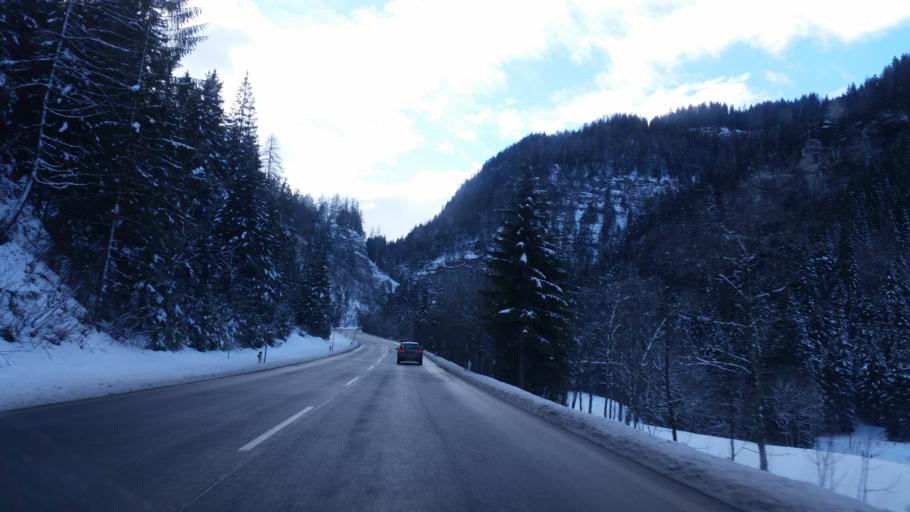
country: AT
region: Salzburg
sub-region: Politischer Bezirk Sankt Johann im Pongau
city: Untertauern
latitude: 47.2987
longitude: 13.5058
